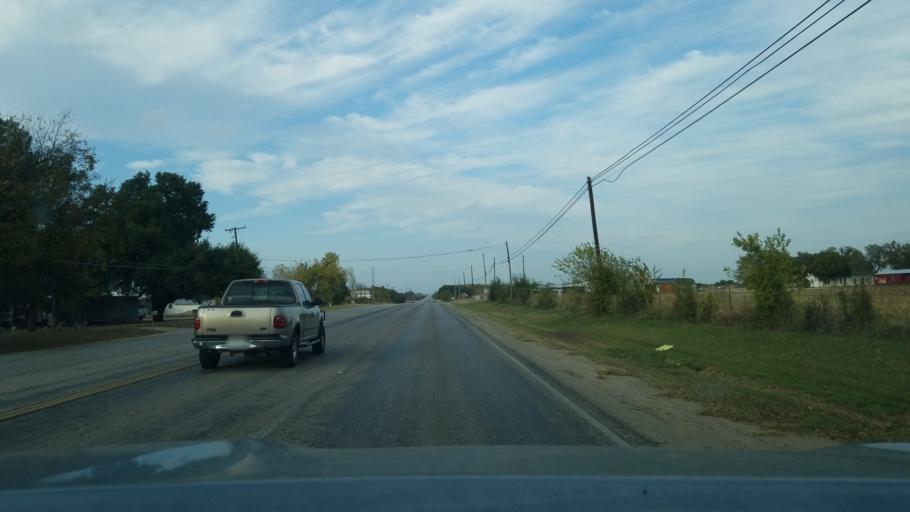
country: US
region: Texas
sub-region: Brown County
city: Early
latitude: 31.7515
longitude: -98.9621
